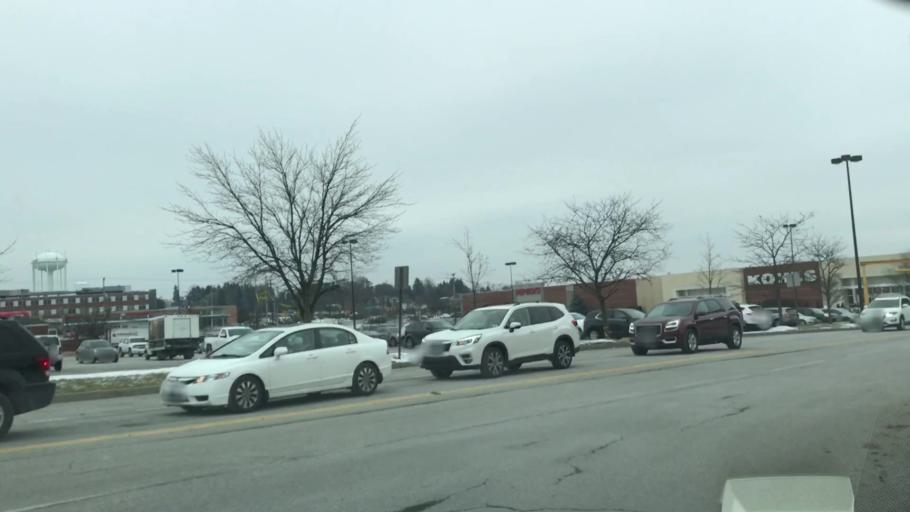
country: US
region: Pennsylvania
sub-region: Allegheny County
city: Rennerdale
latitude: 40.4481
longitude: -80.1608
